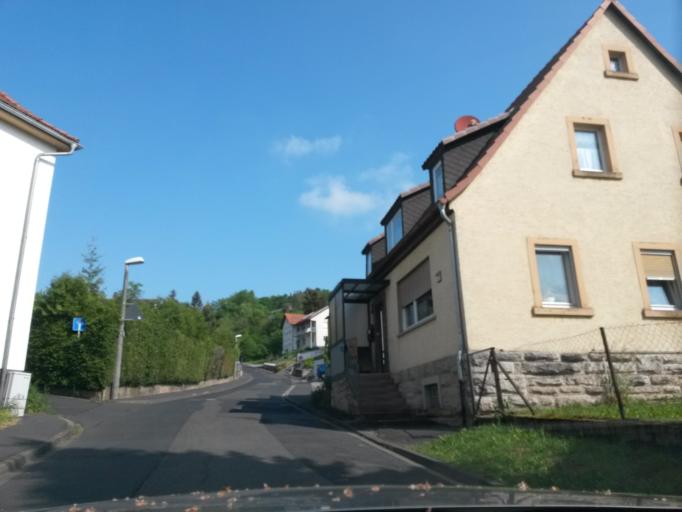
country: DE
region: Bavaria
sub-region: Regierungsbezirk Unterfranken
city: Bad Kissingen
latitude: 50.1868
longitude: 10.0908
